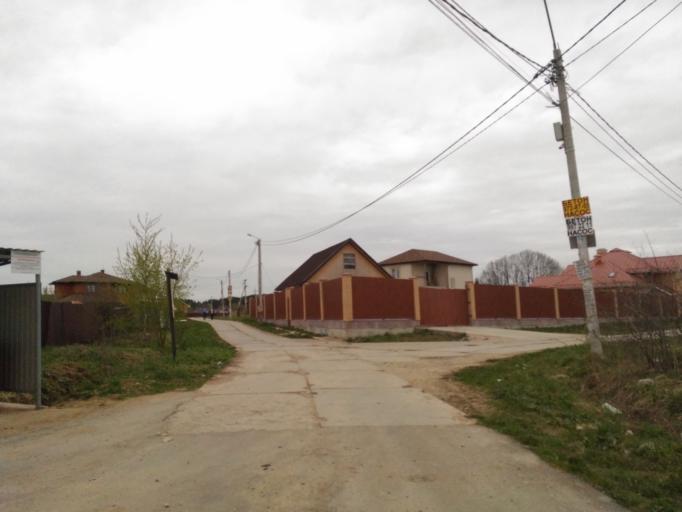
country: RU
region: Moskovskaya
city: Dedovsk
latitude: 55.8523
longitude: 37.1338
